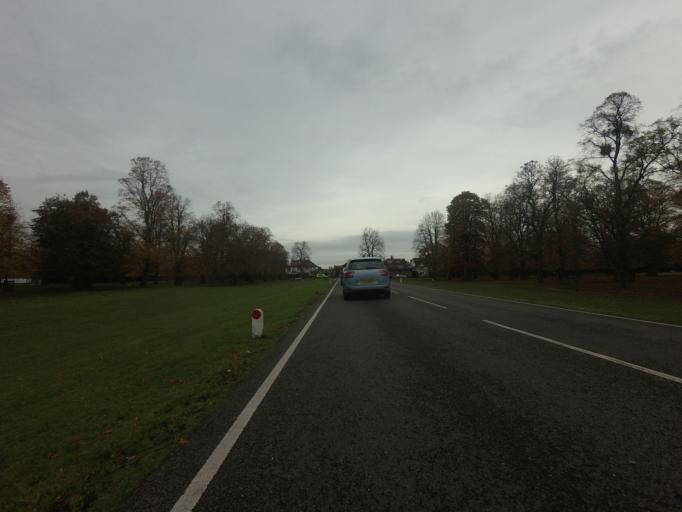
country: GB
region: England
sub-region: Greater London
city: Teddington
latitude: 51.4198
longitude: -0.3337
